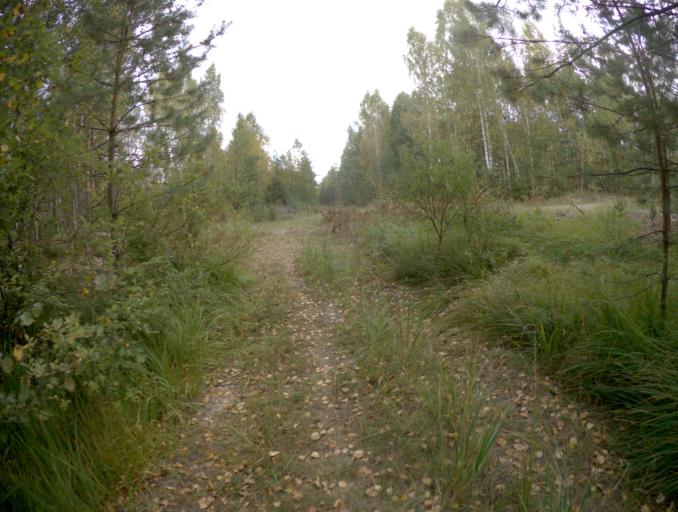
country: RU
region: Vladimir
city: Urshel'skiy
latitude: 55.7428
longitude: 40.0579
